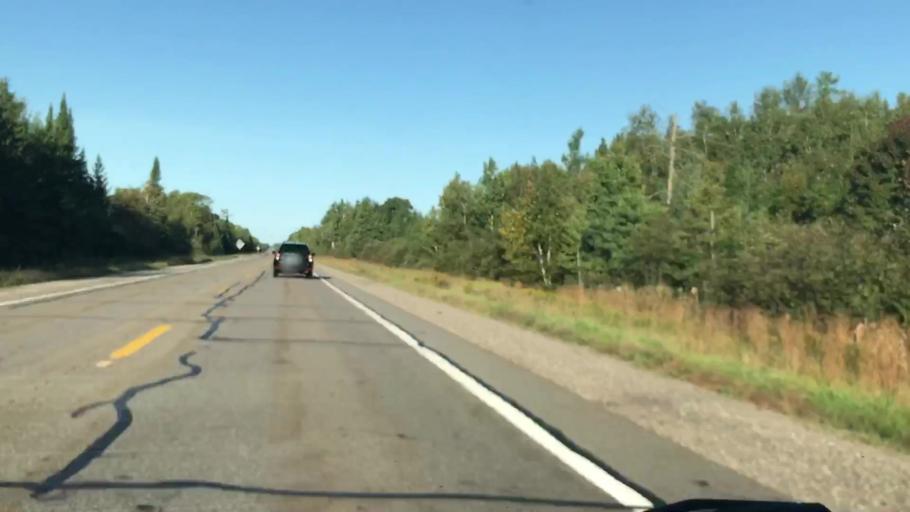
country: US
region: Michigan
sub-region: Chippewa County
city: Sault Ste. Marie
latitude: 46.3758
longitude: -84.6318
